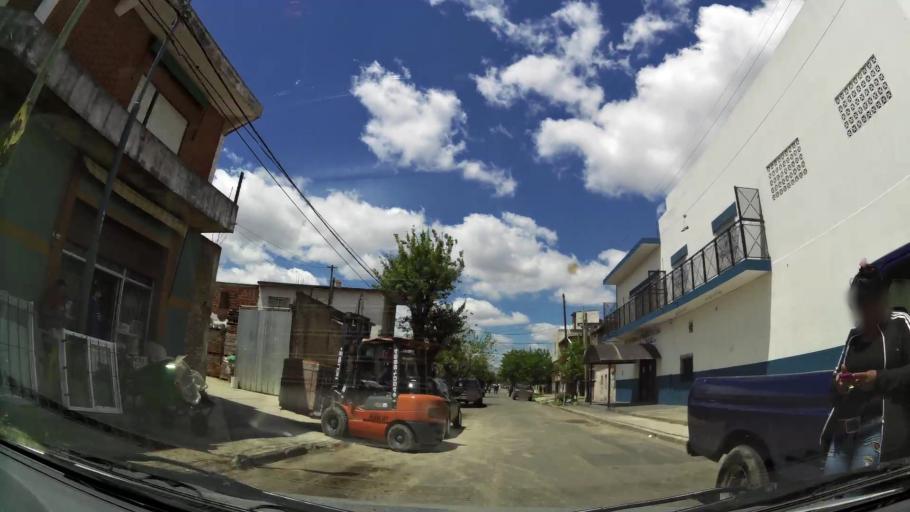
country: AR
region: Buenos Aires
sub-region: Partido de Lanus
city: Lanus
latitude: -34.6974
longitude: -58.4336
